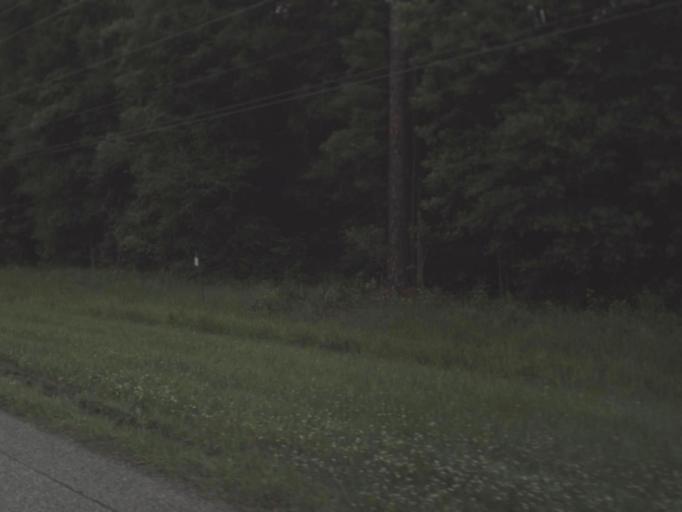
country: US
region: Florida
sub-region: Nassau County
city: Nassau Village-Ratliff
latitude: 30.4820
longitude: -81.7840
